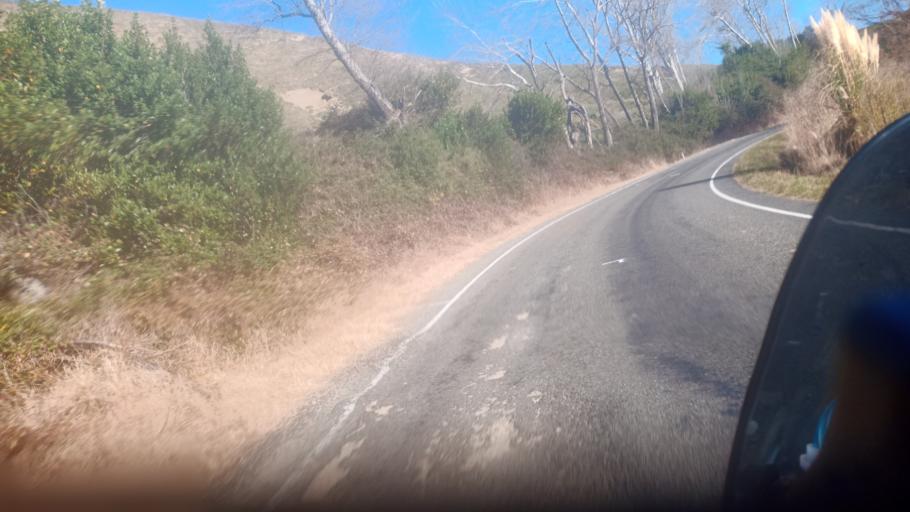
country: NZ
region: Gisborne
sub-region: Gisborne District
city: Gisborne
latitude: -38.5736
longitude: 177.5849
